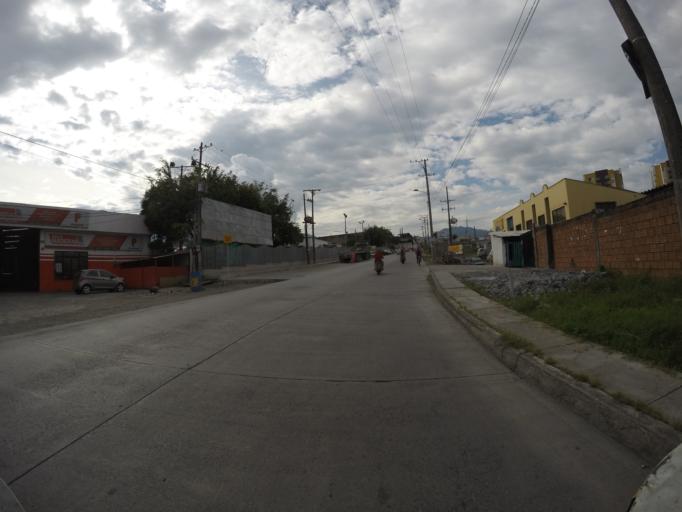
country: CO
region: Risaralda
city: Pereira
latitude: 4.8212
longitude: -75.6889
